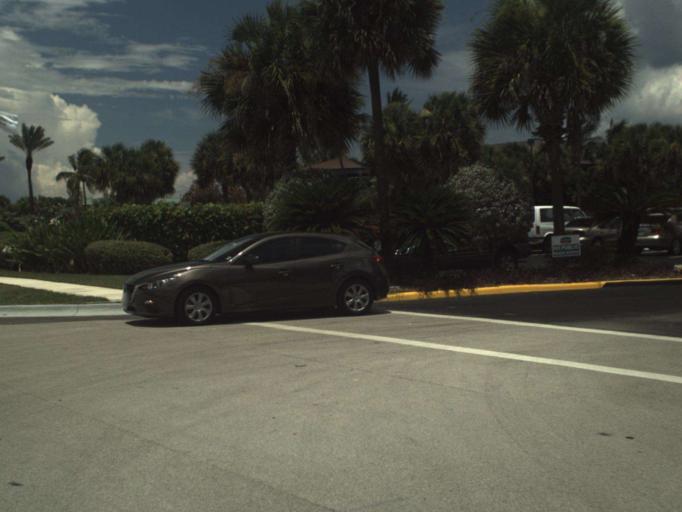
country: US
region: Florida
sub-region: Martin County
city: Jensen Beach
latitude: 27.2647
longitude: -80.2020
